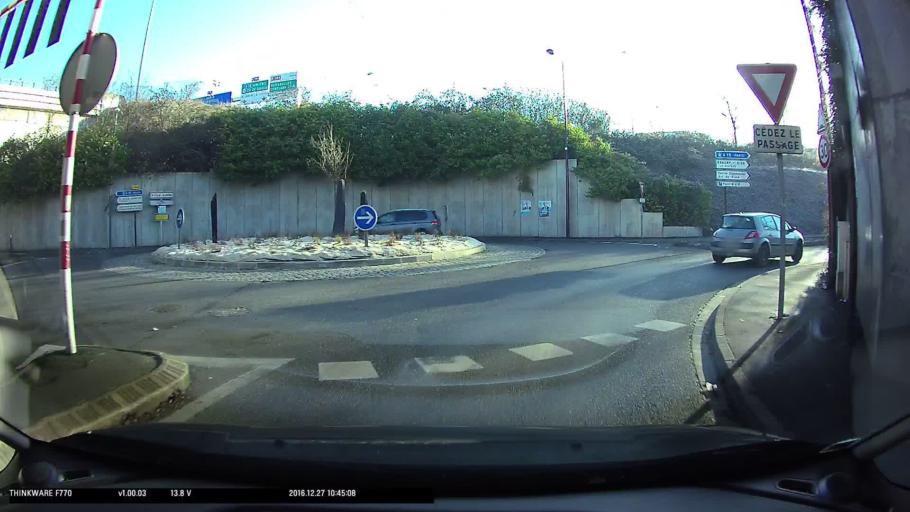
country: FR
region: Ile-de-France
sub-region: Departement du Val-d'Oise
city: Pontoise
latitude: 49.0339
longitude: 2.1017
